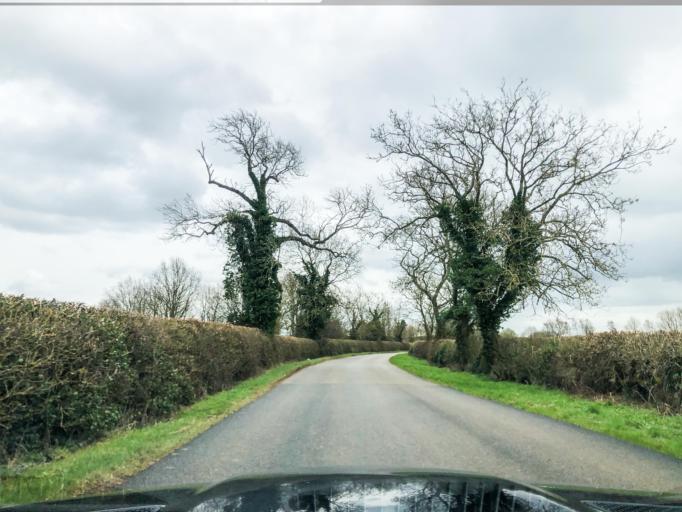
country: GB
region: England
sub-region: Oxfordshire
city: Hook Norton
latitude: 52.0835
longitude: -1.4793
